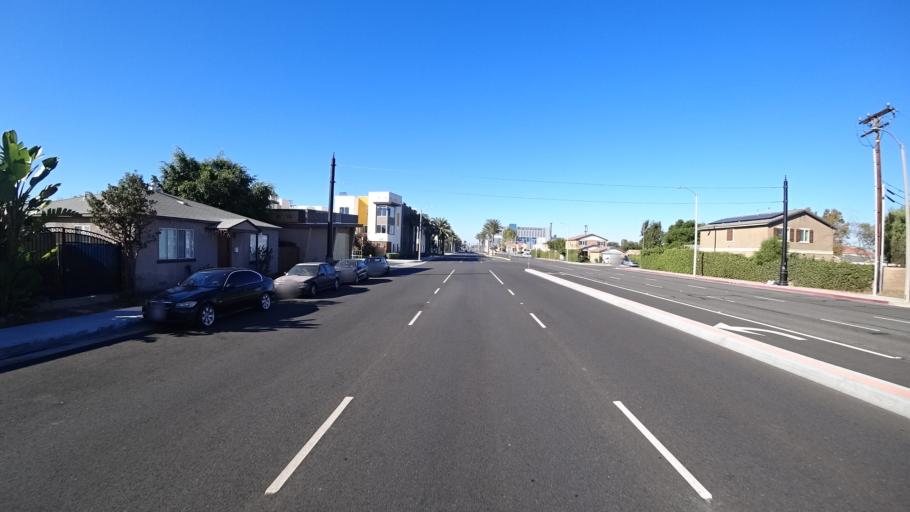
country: US
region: California
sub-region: Orange County
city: Buena Park
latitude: 33.8590
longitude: -117.9900
